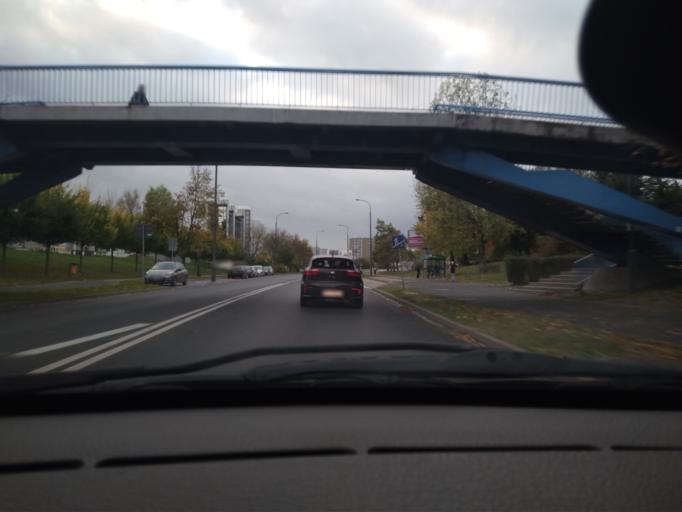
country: PL
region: Greater Poland Voivodeship
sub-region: Poznan
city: Poznan
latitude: 52.4280
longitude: 16.9245
